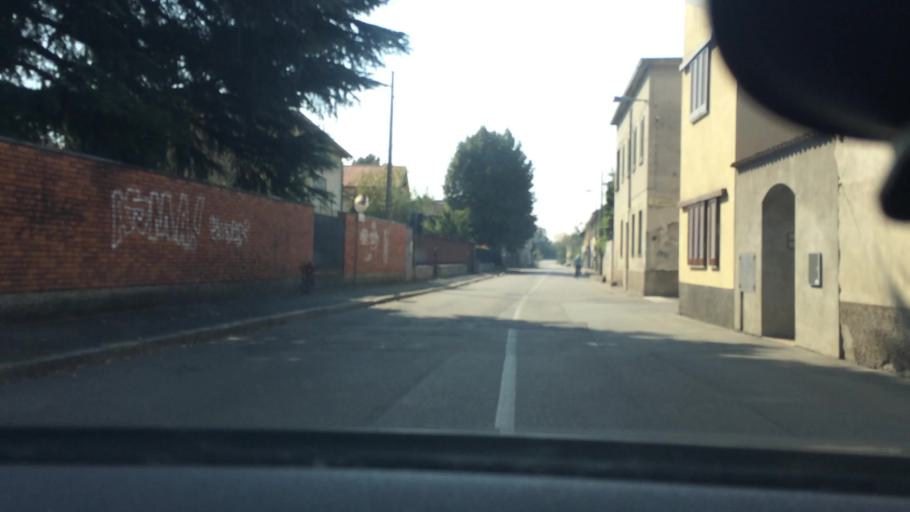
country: IT
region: Lombardy
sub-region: Citta metropolitana di Milano
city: Busto Garolfo
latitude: 45.5440
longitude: 8.8821
